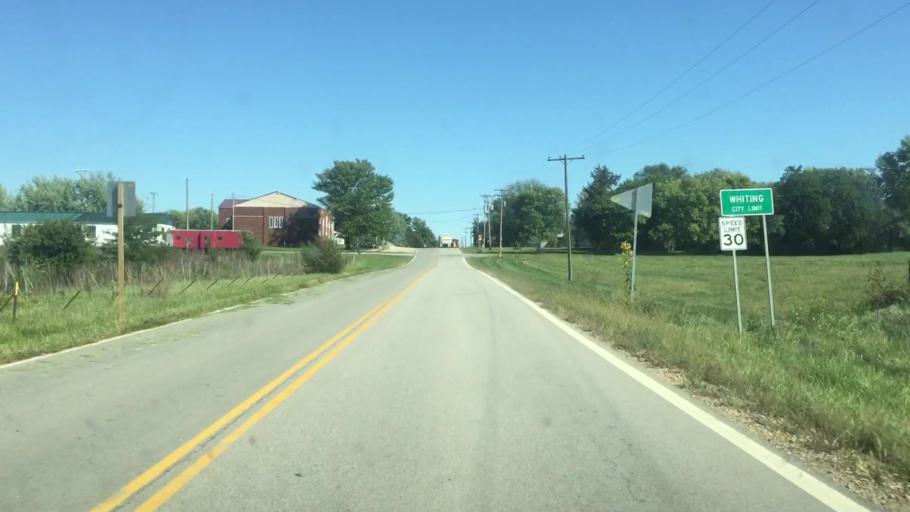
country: US
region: Kansas
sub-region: Brown County
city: Horton
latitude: 39.5930
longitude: -95.6155
